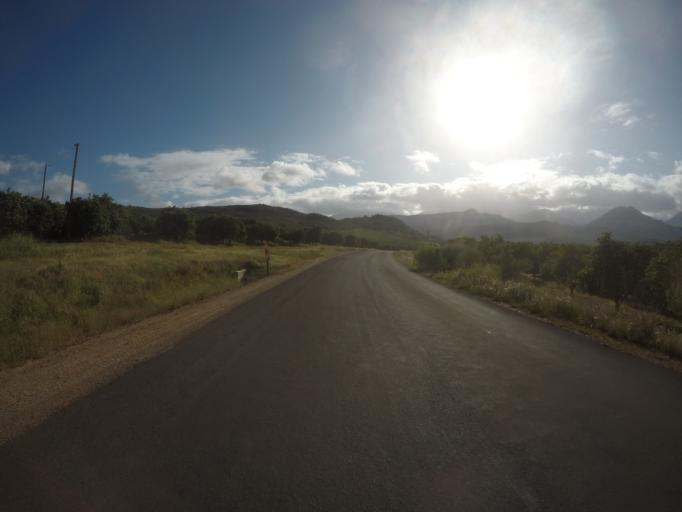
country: ZA
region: Western Cape
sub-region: West Coast District Municipality
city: Clanwilliam
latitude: -32.4321
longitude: 18.9488
